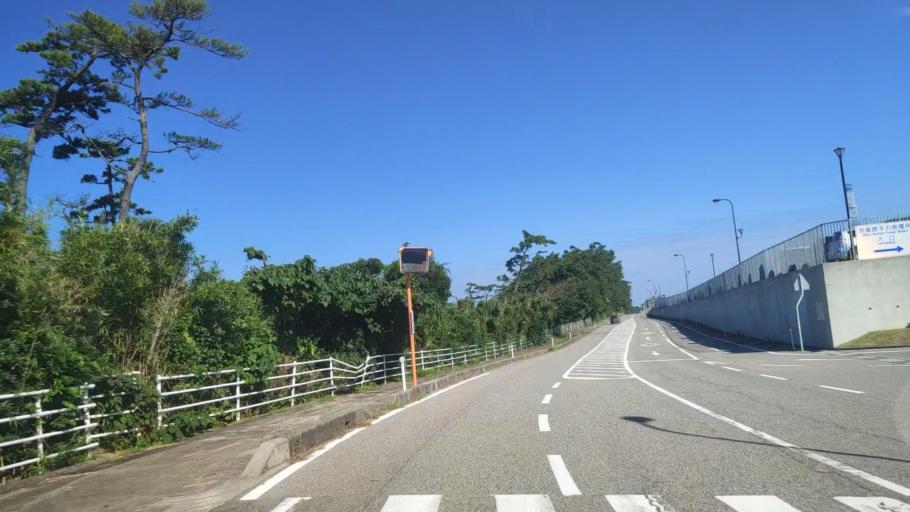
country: JP
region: Ishikawa
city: Hakui
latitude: 37.0559
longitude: 136.7242
